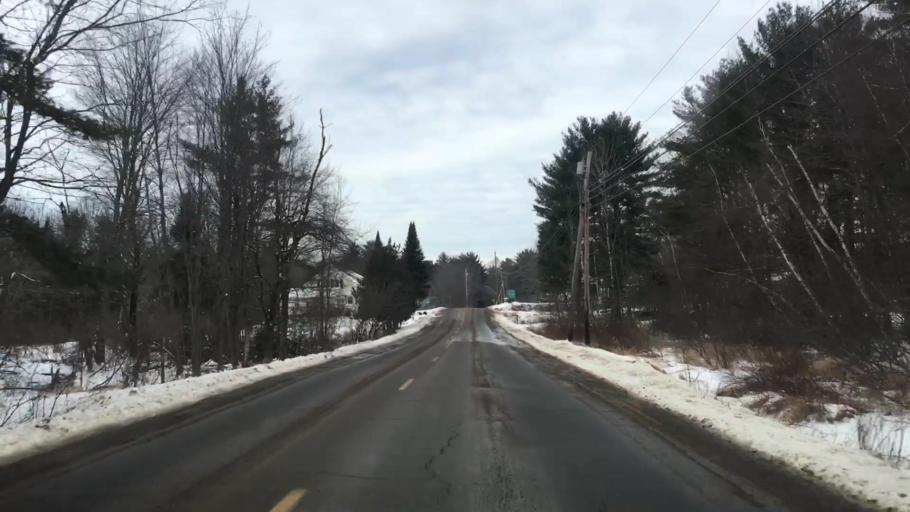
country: US
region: Maine
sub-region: Kennebec County
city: Chelsea
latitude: 44.2695
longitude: -69.6525
